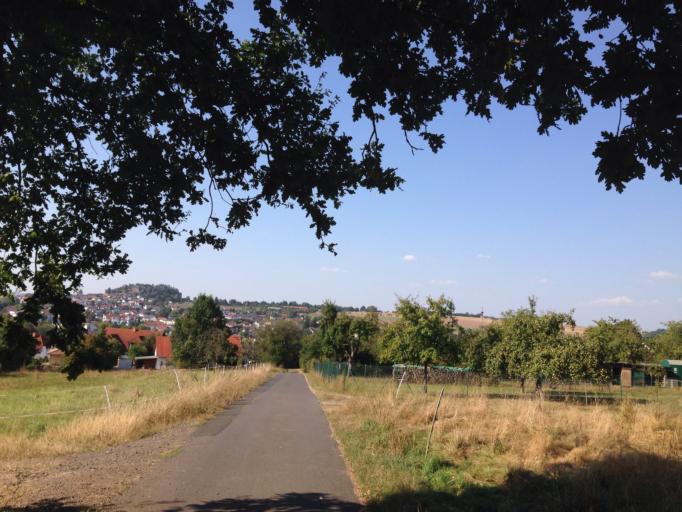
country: DE
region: Hesse
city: Staufenberg
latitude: 50.6537
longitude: 8.7450
